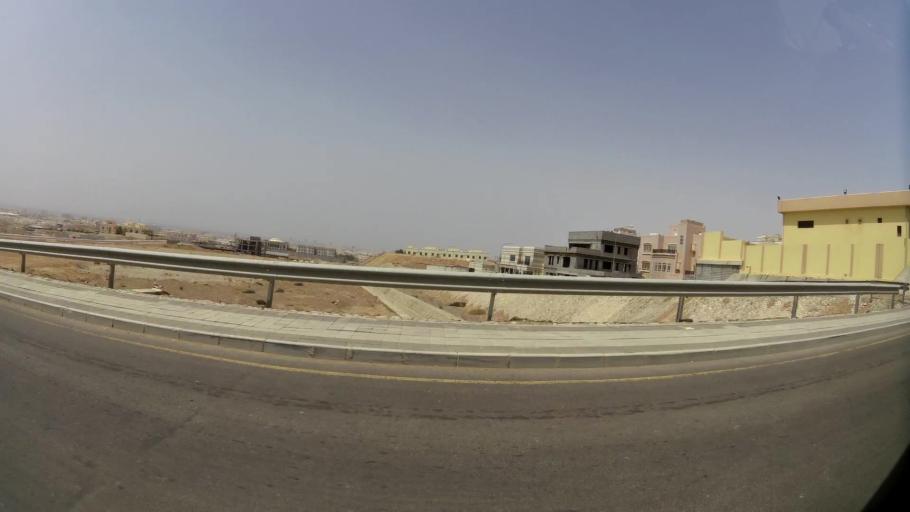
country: OM
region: Muhafazat Masqat
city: Bawshar
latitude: 23.5526
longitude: 58.3936
